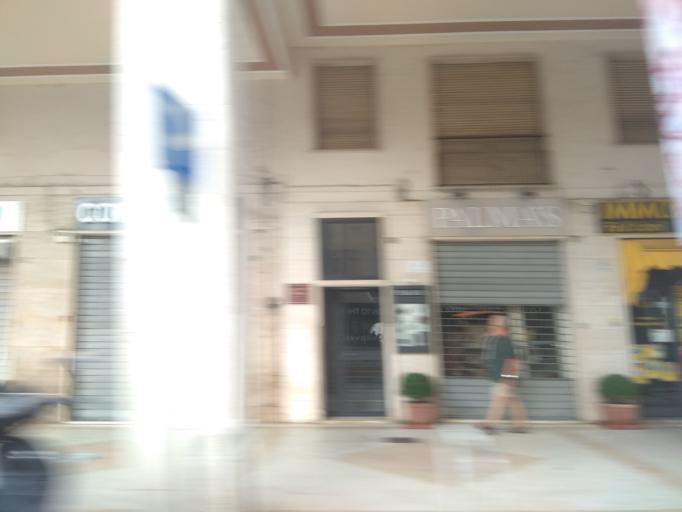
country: IT
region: Latium
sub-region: Citta metropolitana di Roma Capitale
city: Civitavecchia
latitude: 42.0940
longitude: 11.7905
